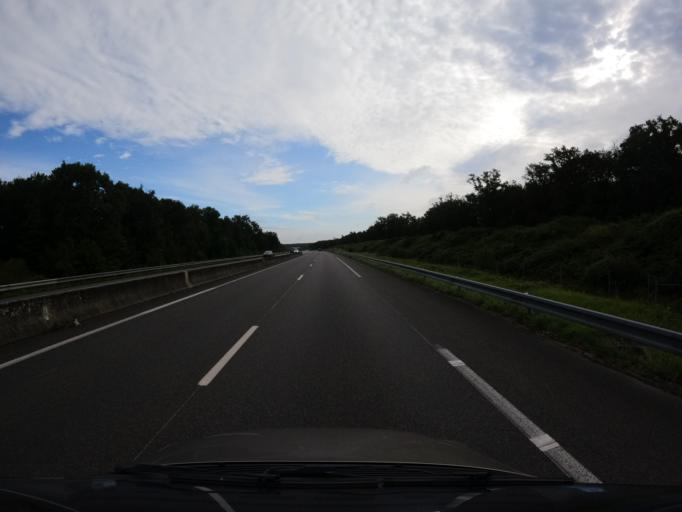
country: FR
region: Centre
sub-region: Departement d'Indre-et-Loire
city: Langeais
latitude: 47.3272
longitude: 0.3425
